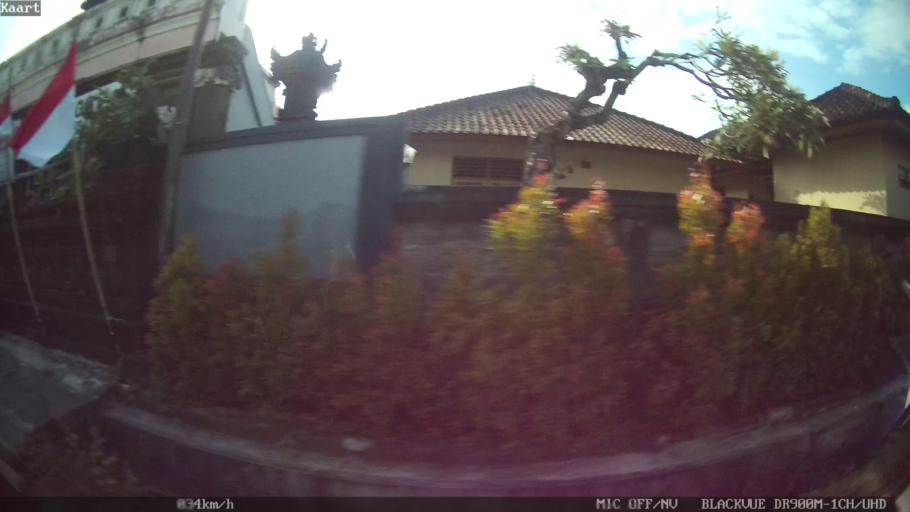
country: ID
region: Bali
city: Kuta
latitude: -8.7100
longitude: 115.1894
